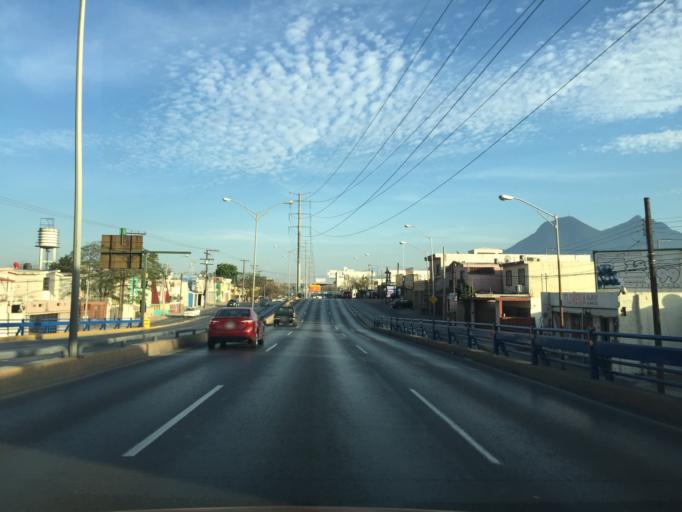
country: MX
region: Nuevo Leon
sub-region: San Nicolas de los Garza
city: San Nicolas de los Garza
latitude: 25.7150
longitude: -100.2829
